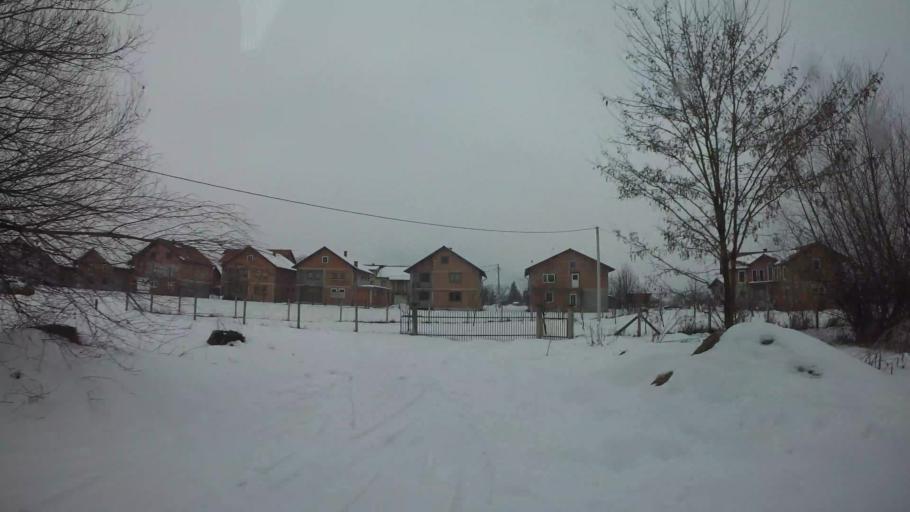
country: BA
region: Federation of Bosnia and Herzegovina
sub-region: Kanton Sarajevo
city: Sarajevo
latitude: 43.8442
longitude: 18.2904
